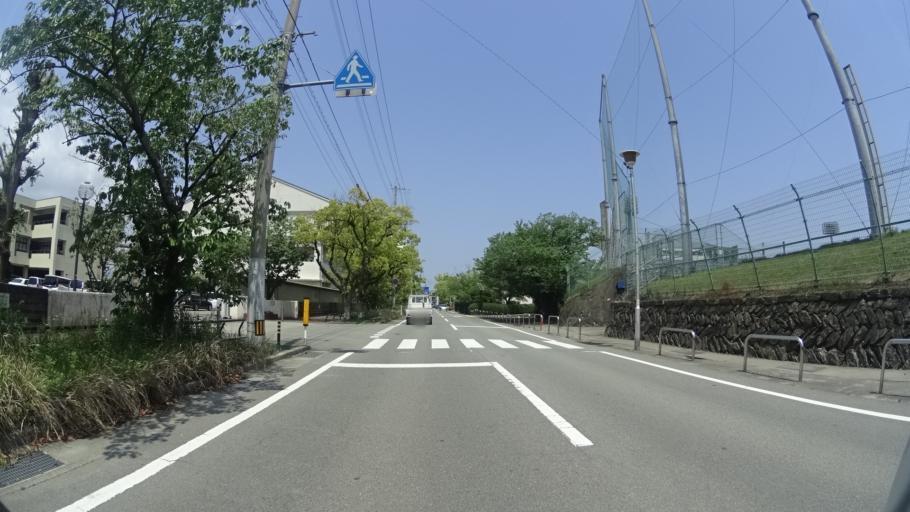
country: JP
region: Tokushima
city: Tokushima-shi
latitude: 34.0732
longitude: 134.5130
